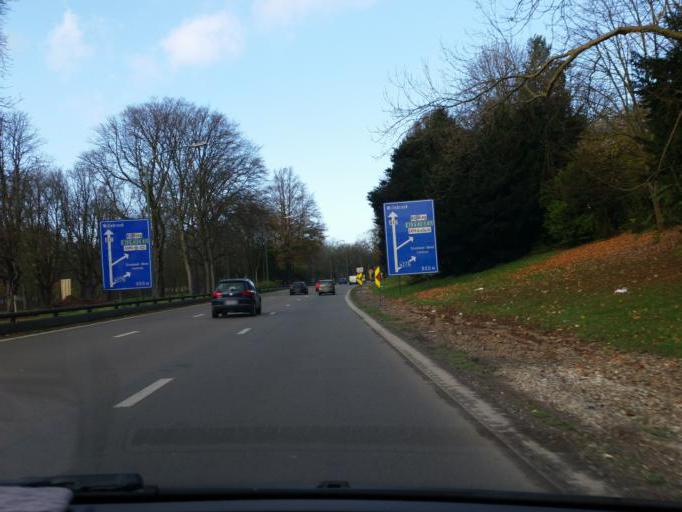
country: BE
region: Flanders
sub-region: Provincie Vlaams-Brabant
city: Bever
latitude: 50.8968
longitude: 4.3509
